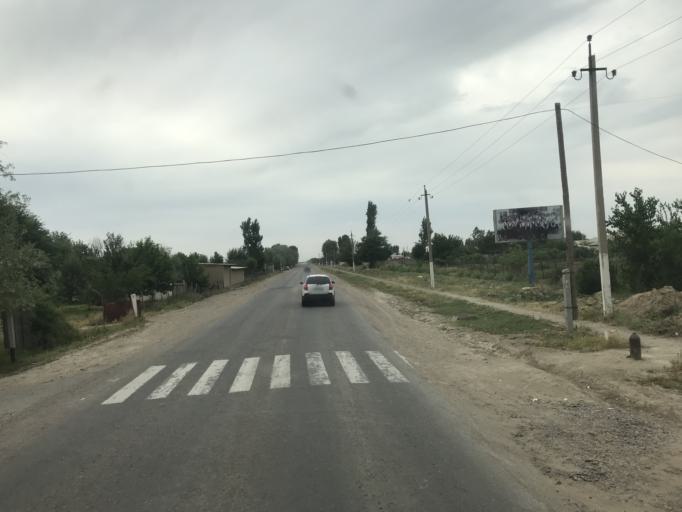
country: KZ
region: Ongtustik Qazaqstan
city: Asykata
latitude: 40.9040
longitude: 68.3559
